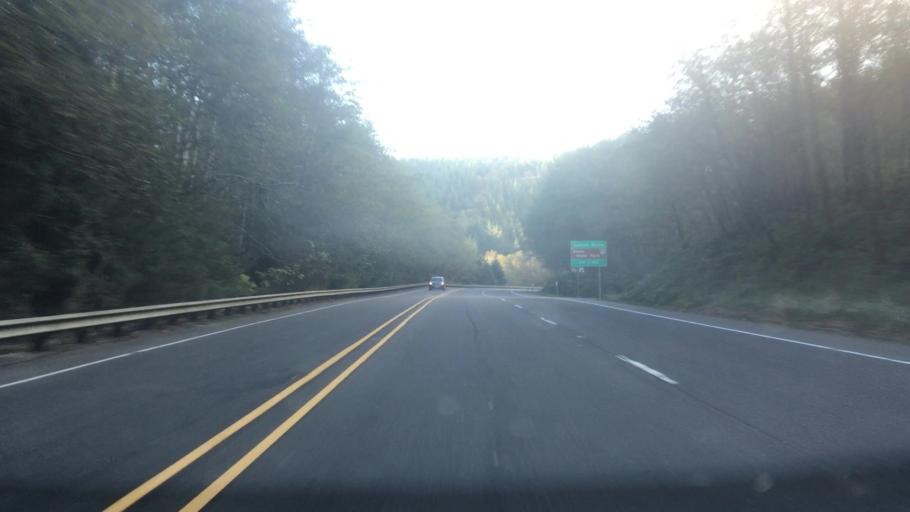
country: US
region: Oregon
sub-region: Clatsop County
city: Cannon Beach
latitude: 45.9179
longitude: -123.9383
